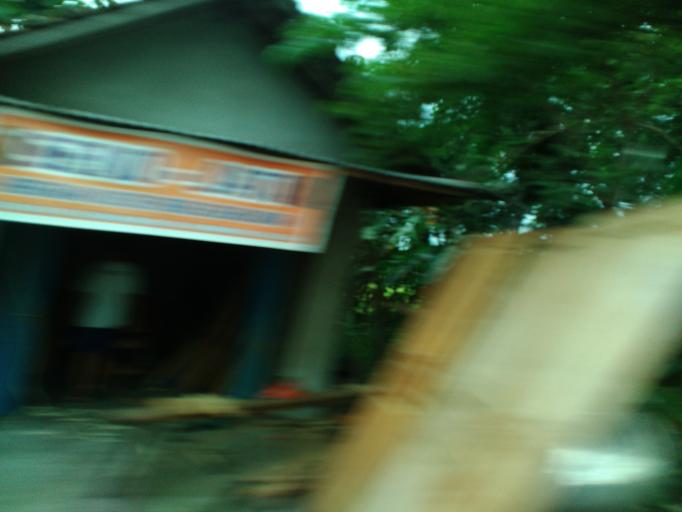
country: ID
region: Central Java
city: Gatak
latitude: -7.5904
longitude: 110.7057
